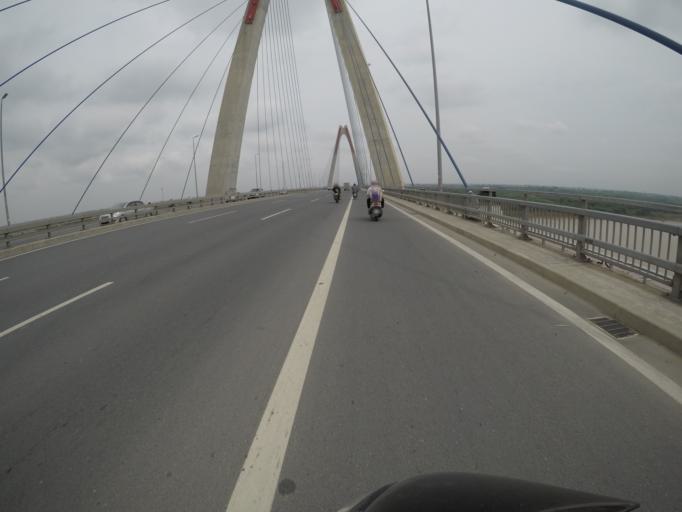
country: VN
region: Ha Noi
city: Tay Ho
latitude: 21.0960
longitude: 105.8223
